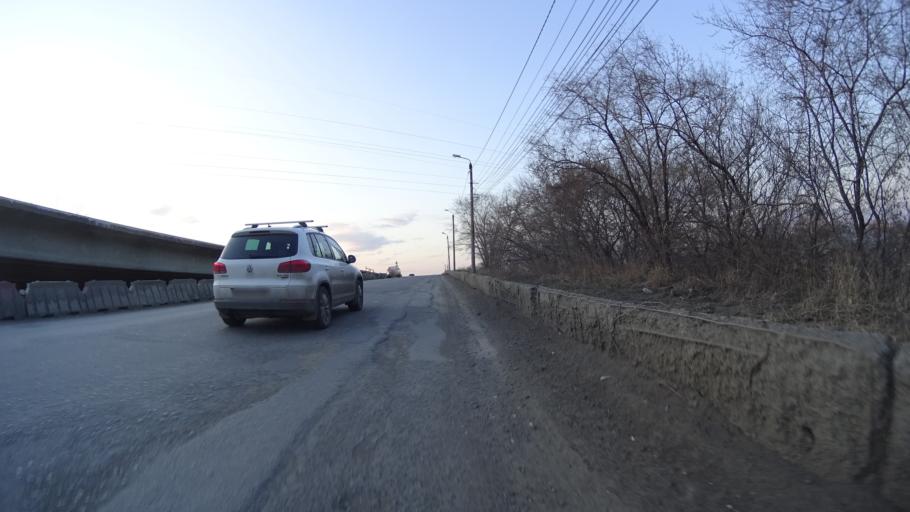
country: RU
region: Chelyabinsk
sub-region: Gorod Chelyabinsk
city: Chelyabinsk
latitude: 55.1151
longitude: 61.3861
